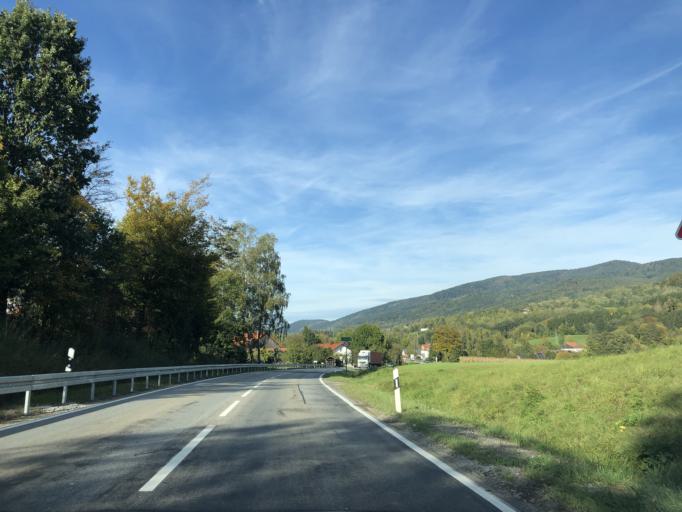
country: DE
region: Bavaria
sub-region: Lower Bavaria
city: Grafling
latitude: 48.8712
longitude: 12.9591
